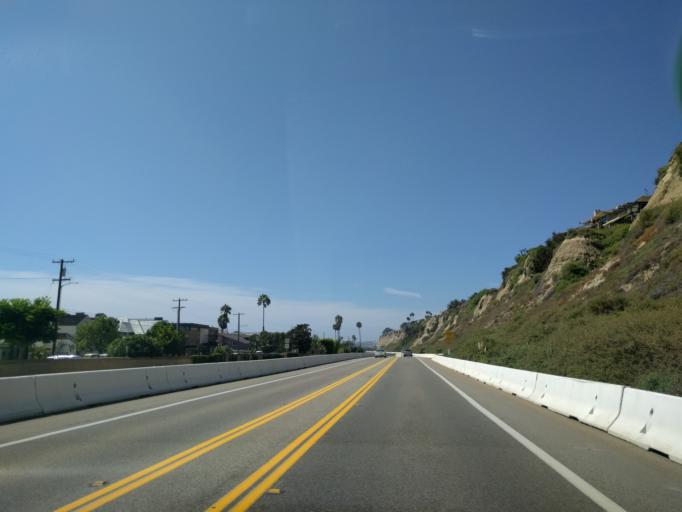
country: US
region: California
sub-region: Orange County
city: Dana Point
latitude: 33.4489
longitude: -117.6553
